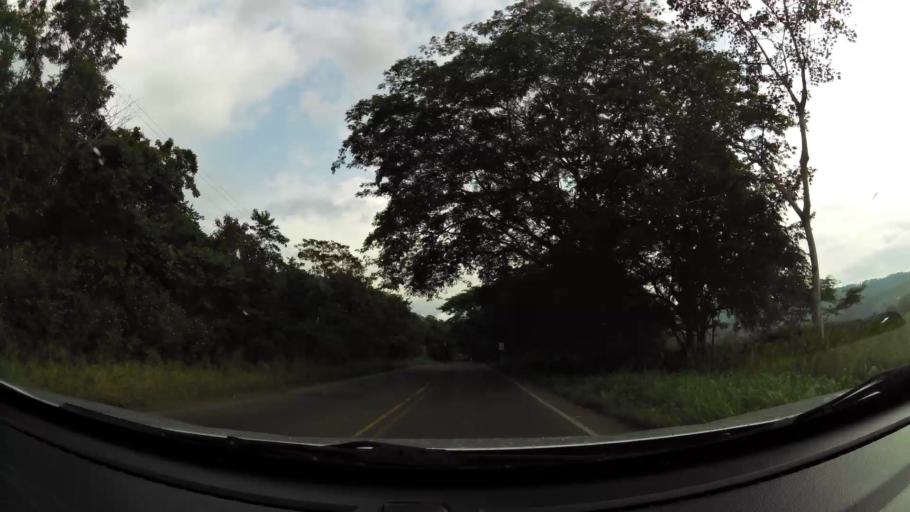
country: CR
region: Guanacaste
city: Juntas
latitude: 10.1990
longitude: -84.9567
